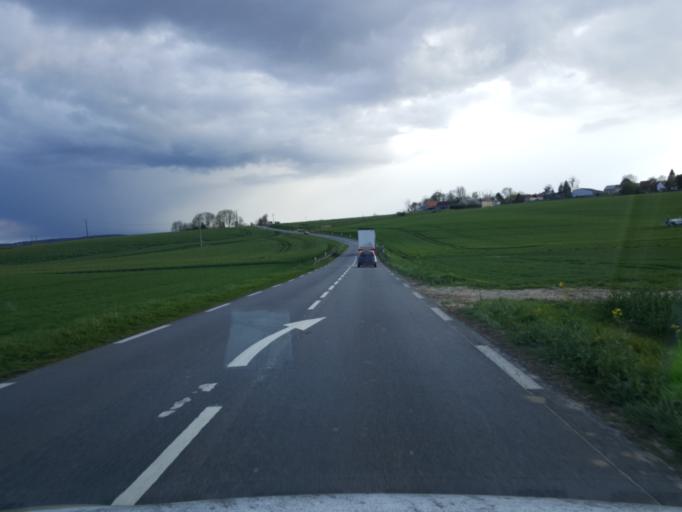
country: FR
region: Ile-de-France
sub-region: Departement du Val-d'Oise
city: Magny-en-Vexin
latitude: 49.0775
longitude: 1.7832
